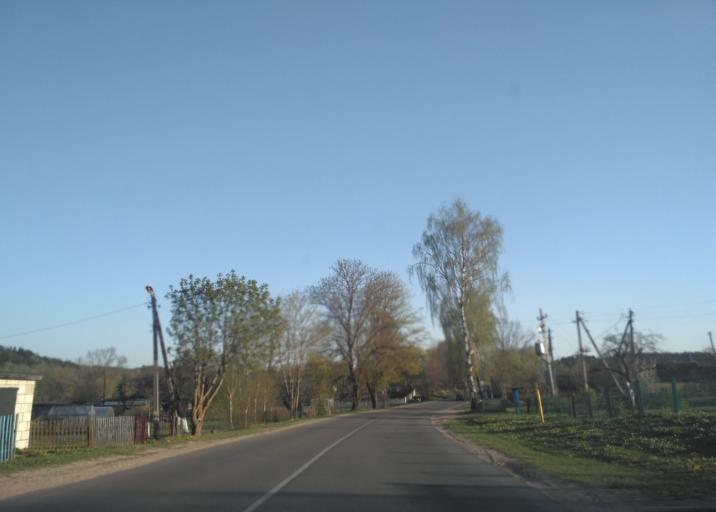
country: BY
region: Minsk
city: Pyatryshki
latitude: 54.1150
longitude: 27.1924
